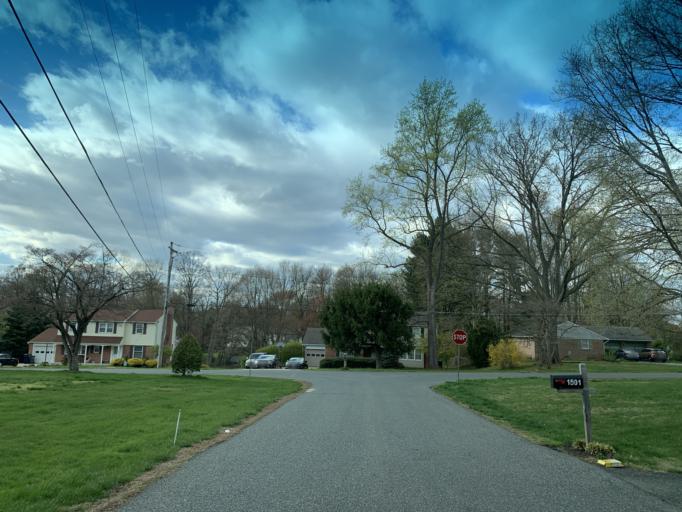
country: US
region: Maryland
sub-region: Harford County
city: South Bel Air
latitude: 39.5422
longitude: -76.3152
